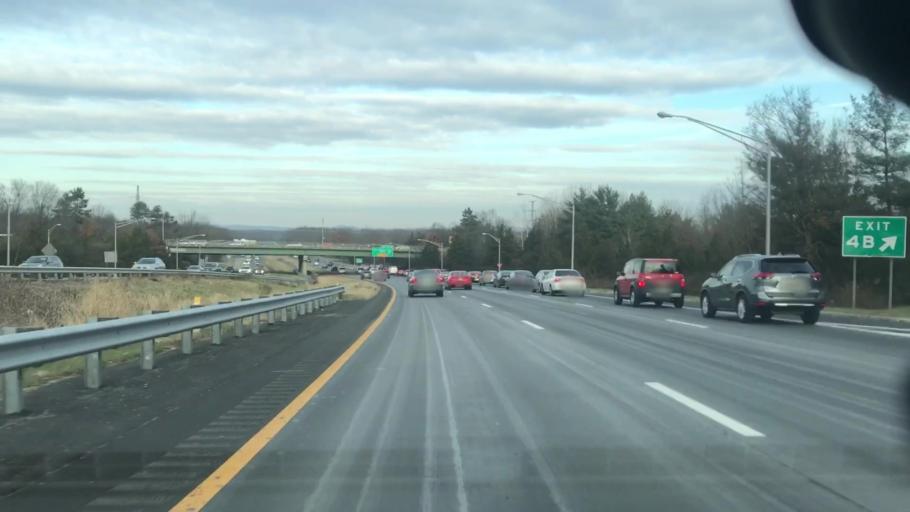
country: US
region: New Jersey
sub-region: Essex County
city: West Caldwell
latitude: 40.8241
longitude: -74.3194
